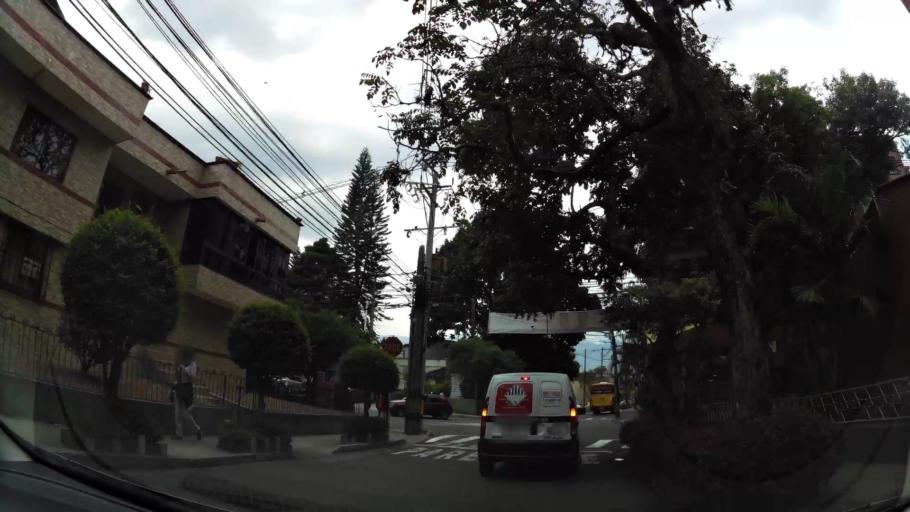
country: CO
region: Antioquia
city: Envigado
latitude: 6.1656
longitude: -75.5907
